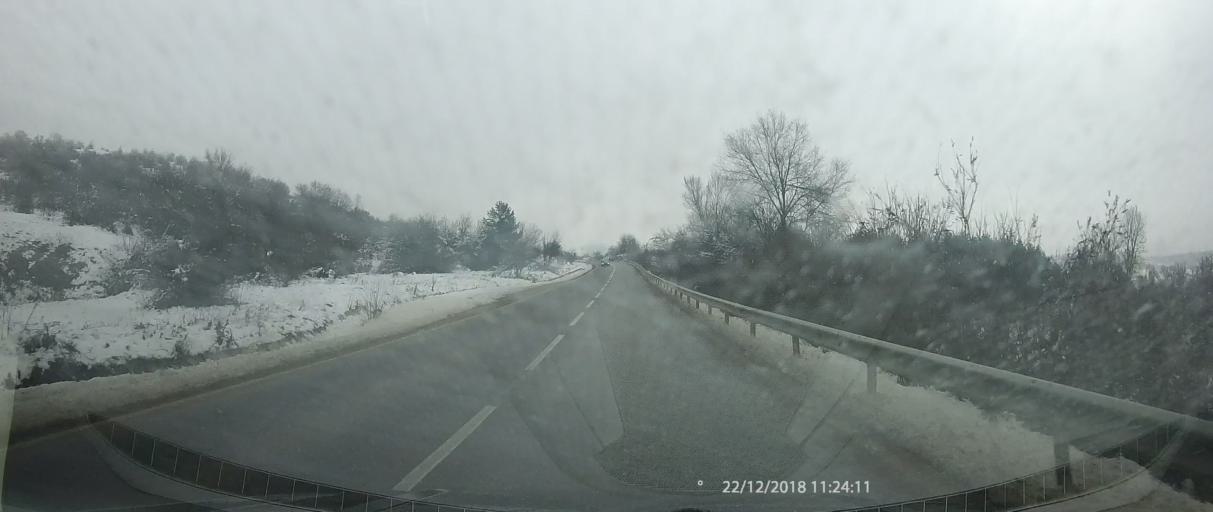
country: BG
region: Kyustendil
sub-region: Obshtina Boboshevo
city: Boboshevo
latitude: 42.2512
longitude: 22.8879
